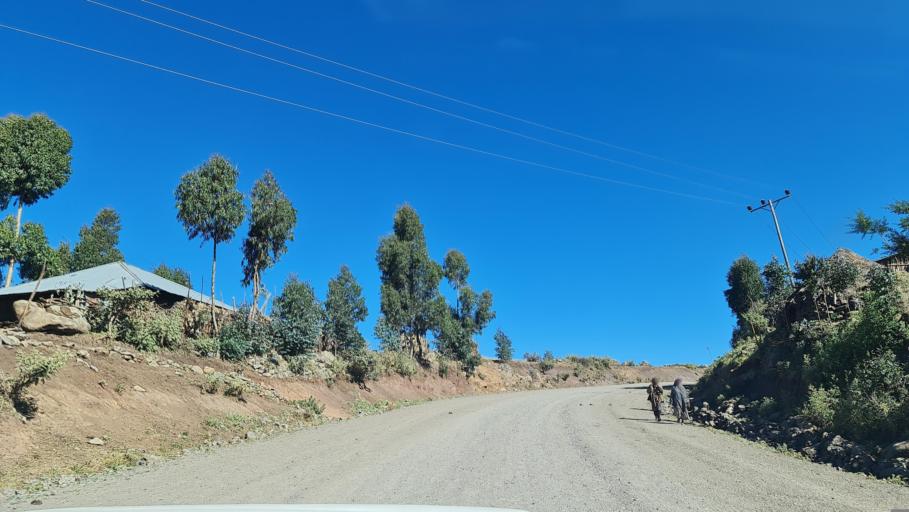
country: ET
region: Amhara
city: Debark'
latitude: 13.1178
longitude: 38.1546
